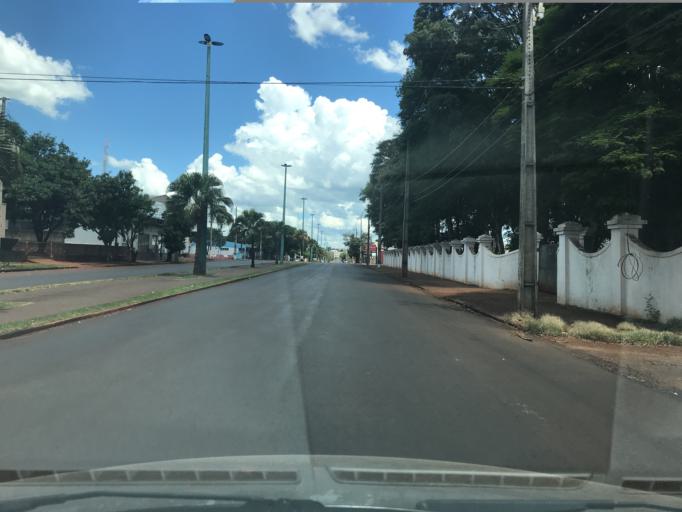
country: BR
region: Parana
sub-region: Palotina
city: Palotina
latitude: -24.2727
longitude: -53.8417
